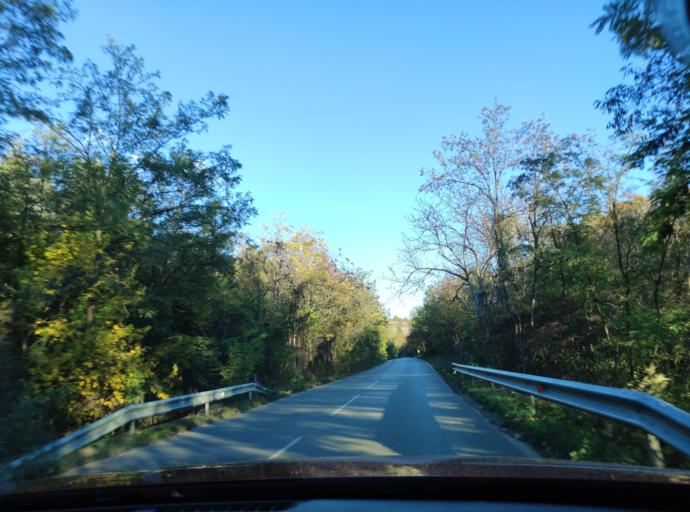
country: BG
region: Montana
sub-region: Obshtina Montana
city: Montana
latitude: 43.4017
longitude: 23.0869
